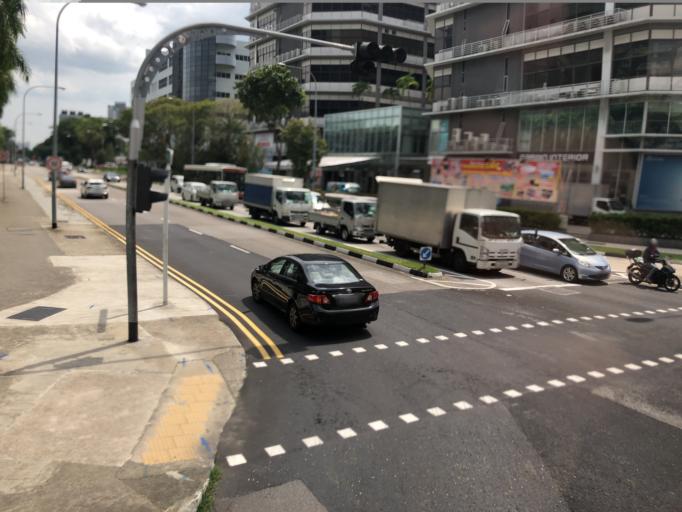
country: SG
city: Singapore
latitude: 1.3169
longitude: 103.8630
